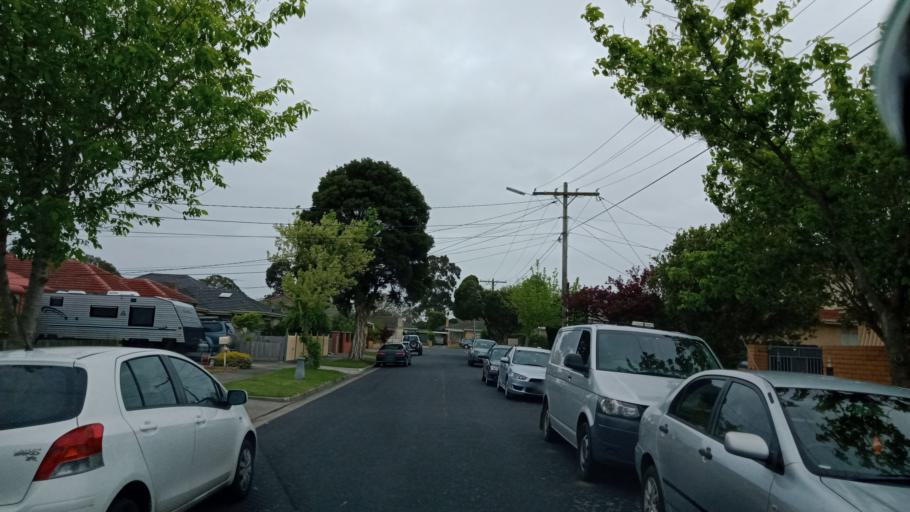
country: AU
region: Victoria
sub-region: Monash
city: Oakleigh South
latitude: -37.9287
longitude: 145.0724
